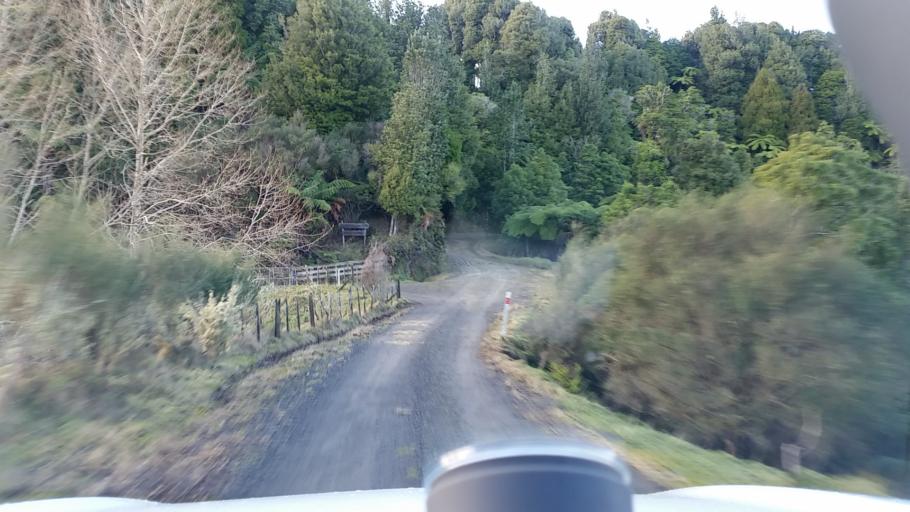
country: NZ
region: Taranaki
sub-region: South Taranaki District
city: Eltham
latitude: -39.4273
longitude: 174.5596
